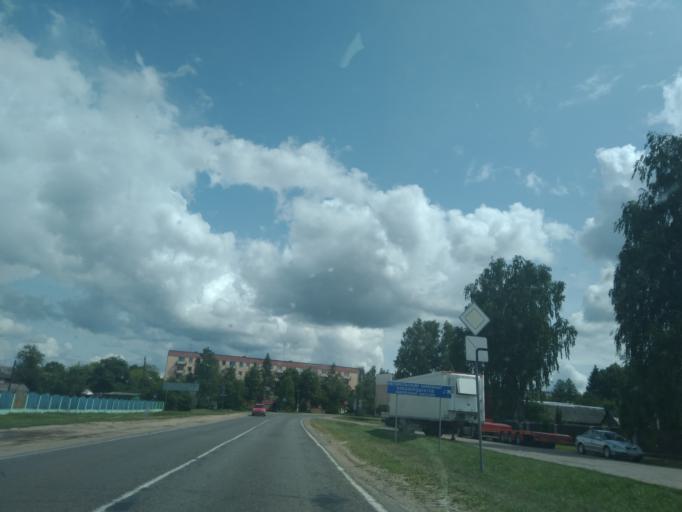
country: BY
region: Minsk
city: Enyerhyetykaw
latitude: 53.5882
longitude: 27.0505
